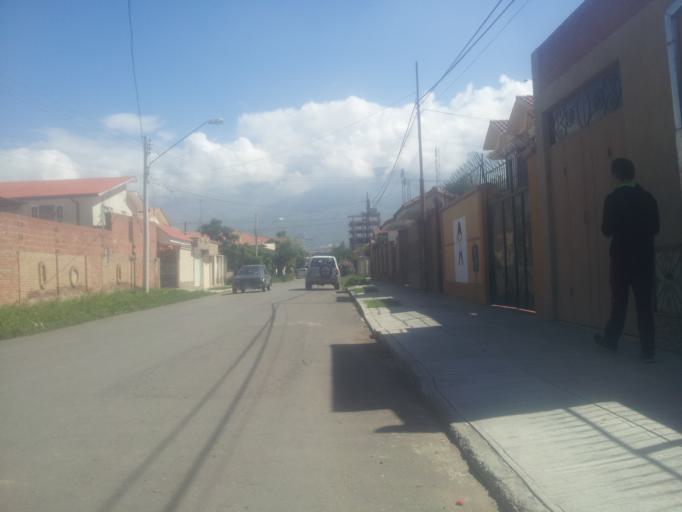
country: BO
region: Cochabamba
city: Cochabamba
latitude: -17.3826
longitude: -66.1728
